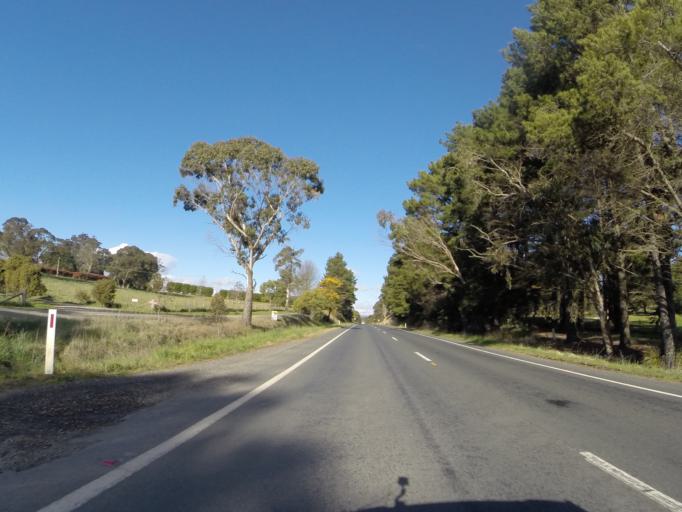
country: AU
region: New South Wales
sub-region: Wingecarribee
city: Moss Vale
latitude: -34.5697
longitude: 150.4415
